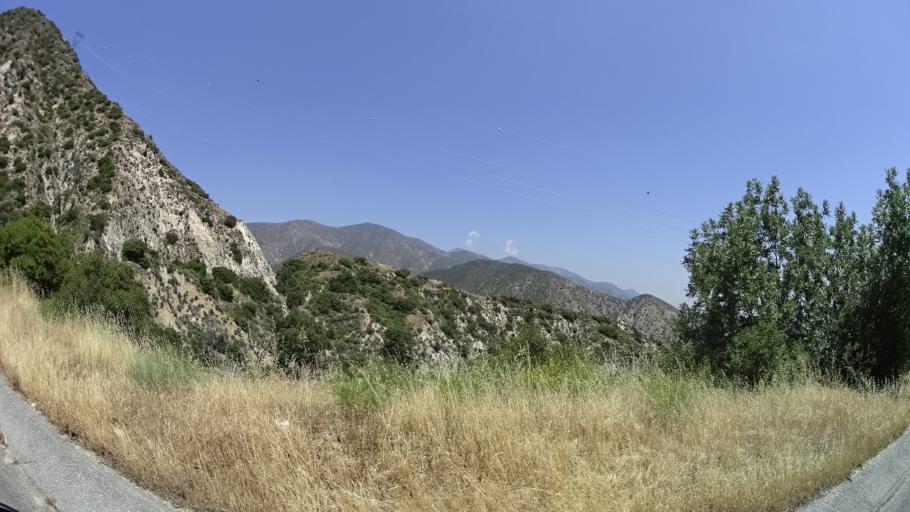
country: US
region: California
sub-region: Los Angeles County
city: La Canada Flintridge
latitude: 34.2262
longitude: -118.1883
